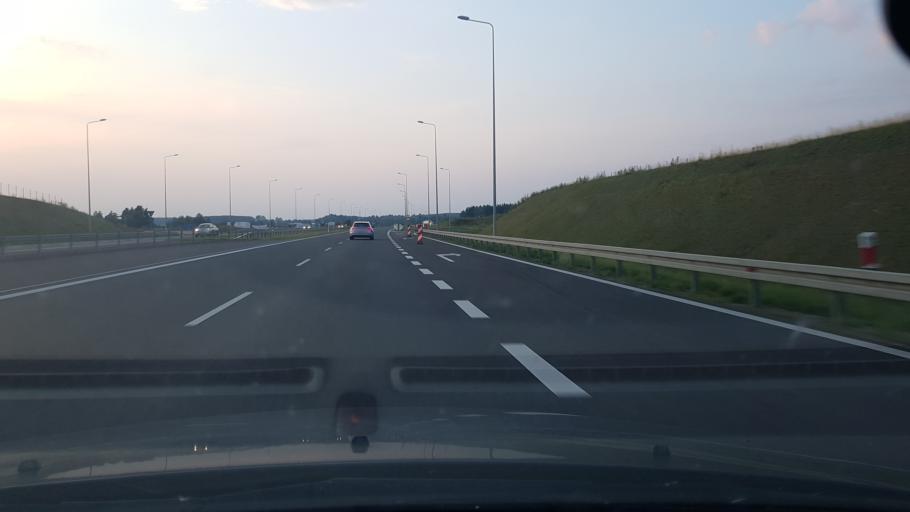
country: PL
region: Warmian-Masurian Voivodeship
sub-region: Powiat nidzicki
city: Nidzica
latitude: 53.2972
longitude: 20.4369
